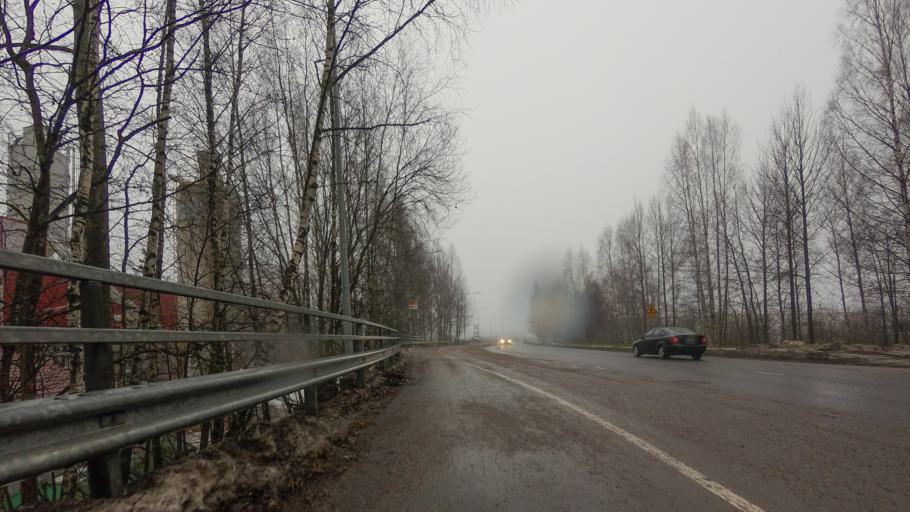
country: FI
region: Uusimaa
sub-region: Helsinki
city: Vantaa
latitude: 60.2148
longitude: 25.0589
